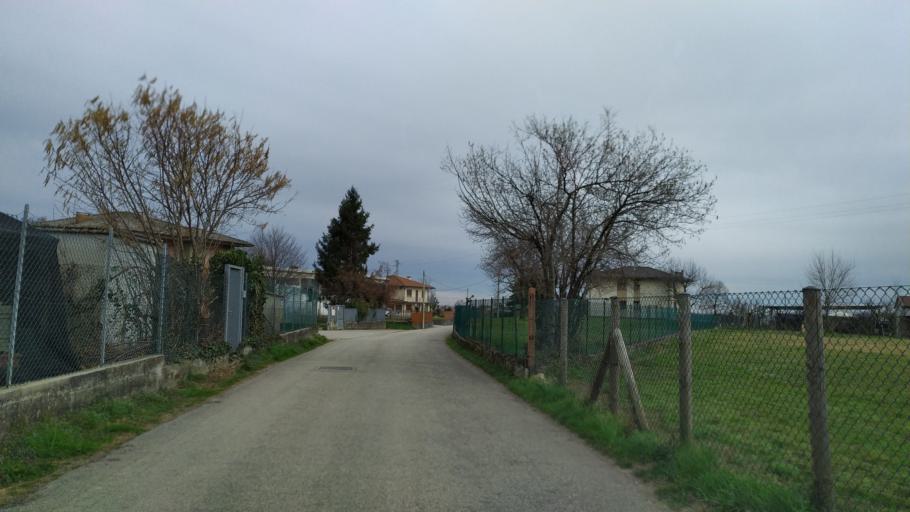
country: IT
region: Veneto
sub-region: Provincia di Vicenza
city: Malo
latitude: 45.6562
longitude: 11.4220
